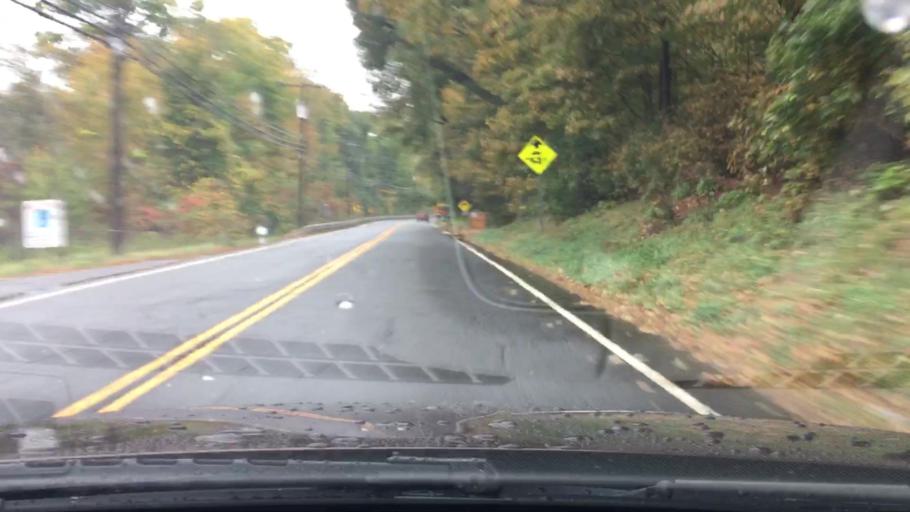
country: US
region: Connecticut
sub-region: Tolland County
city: Ellington
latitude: 41.9284
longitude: -72.4556
